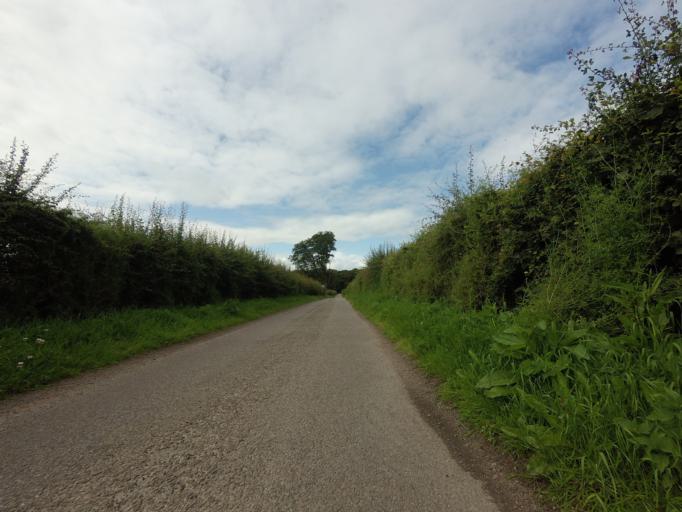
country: GB
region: Scotland
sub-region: Moray
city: Hopeman
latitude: 57.6736
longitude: -3.4081
